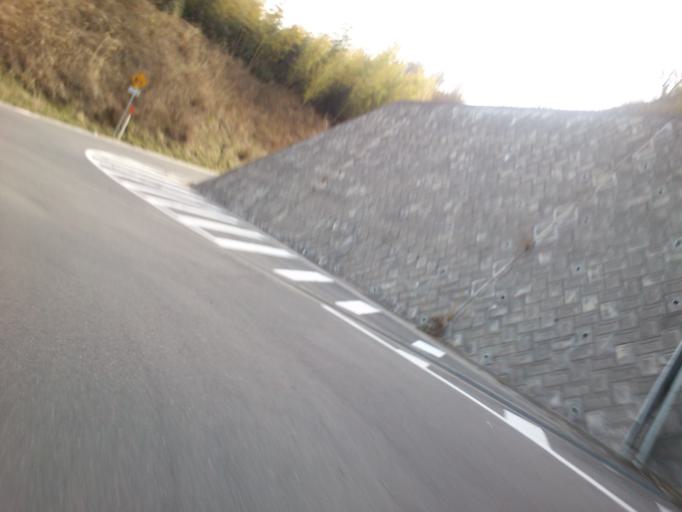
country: JP
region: Kyoto
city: Yawata
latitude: 34.9132
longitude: 135.6506
